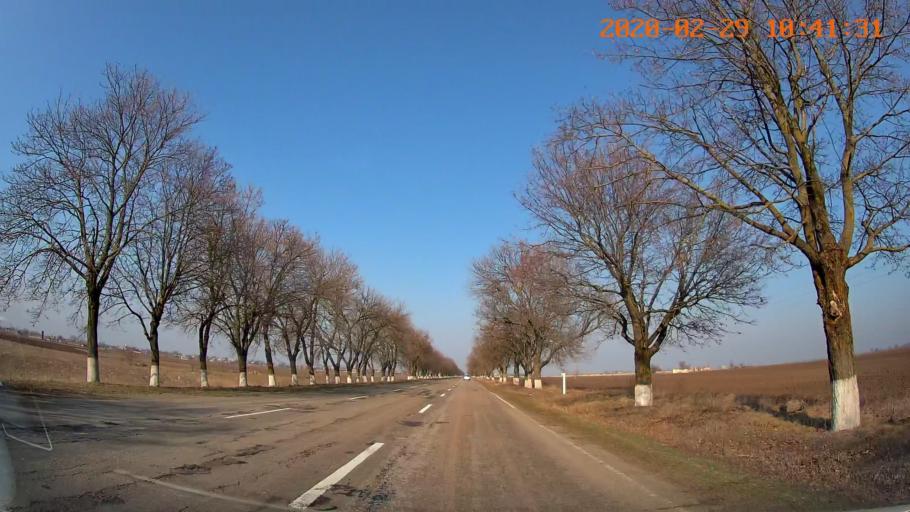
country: MD
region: Telenesti
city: Grigoriopol
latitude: 47.0432
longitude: 29.4239
